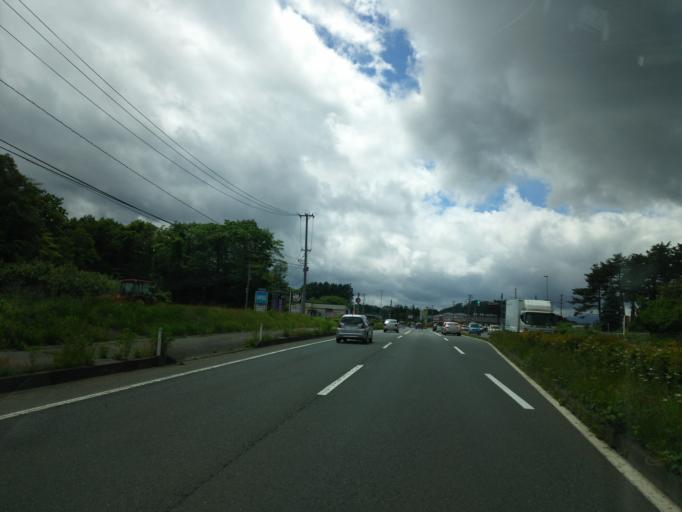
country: JP
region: Iwate
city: Shizukuishi
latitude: 39.7021
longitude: 141.0371
